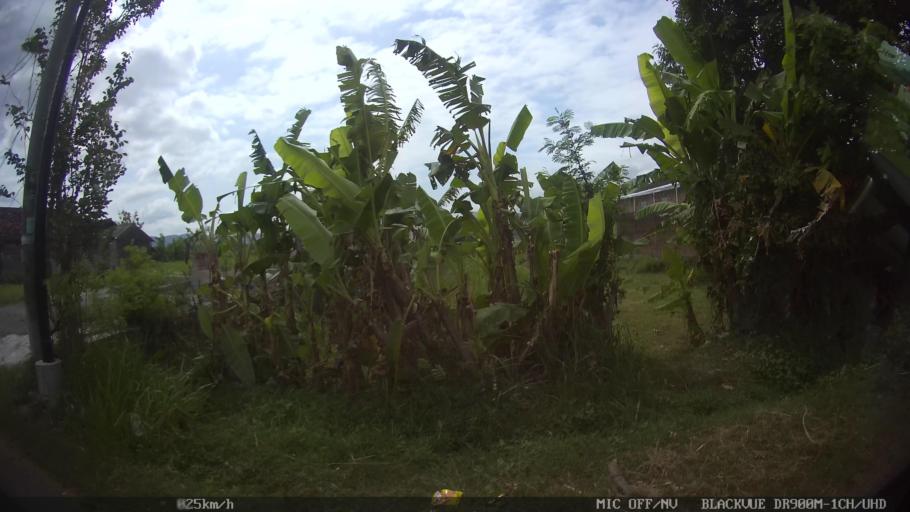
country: ID
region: Daerah Istimewa Yogyakarta
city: Depok
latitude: -7.8278
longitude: 110.4636
